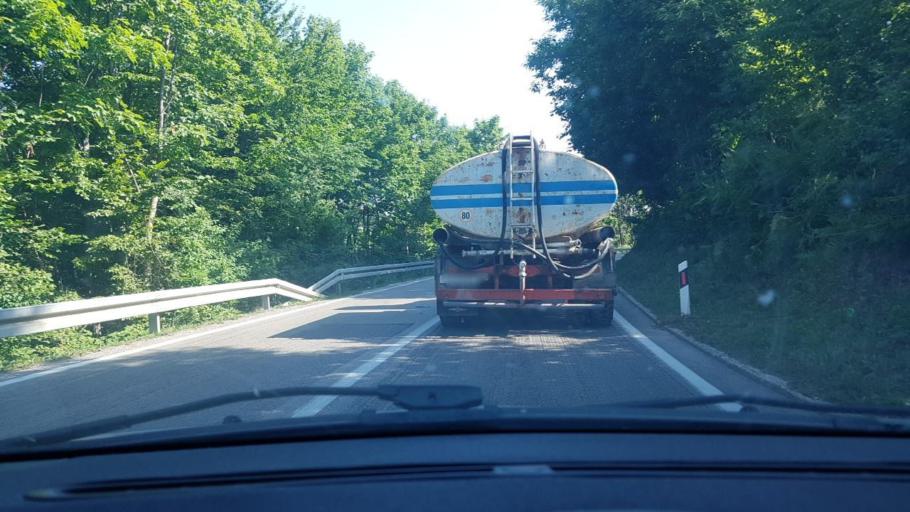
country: BA
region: Federation of Bosnia and Herzegovina
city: Skokovi
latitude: 45.0288
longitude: 15.9117
